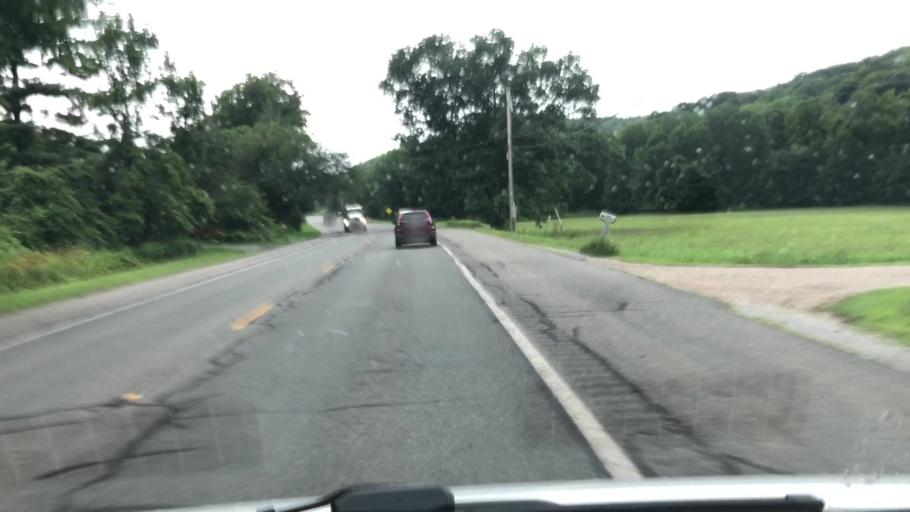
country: US
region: Massachusetts
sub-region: Berkshire County
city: Williamstown
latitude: 42.6354
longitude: -73.2263
